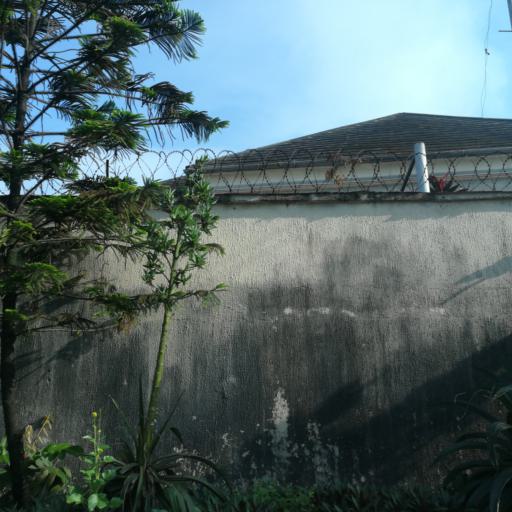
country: NG
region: Rivers
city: Port Harcourt
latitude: 4.8065
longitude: 7.0202
